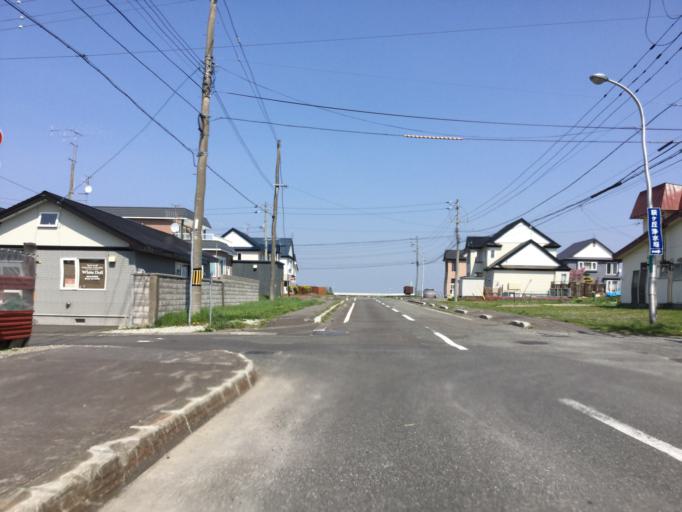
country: JP
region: Hokkaido
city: Wakkanai
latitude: 45.3905
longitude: 141.7242
